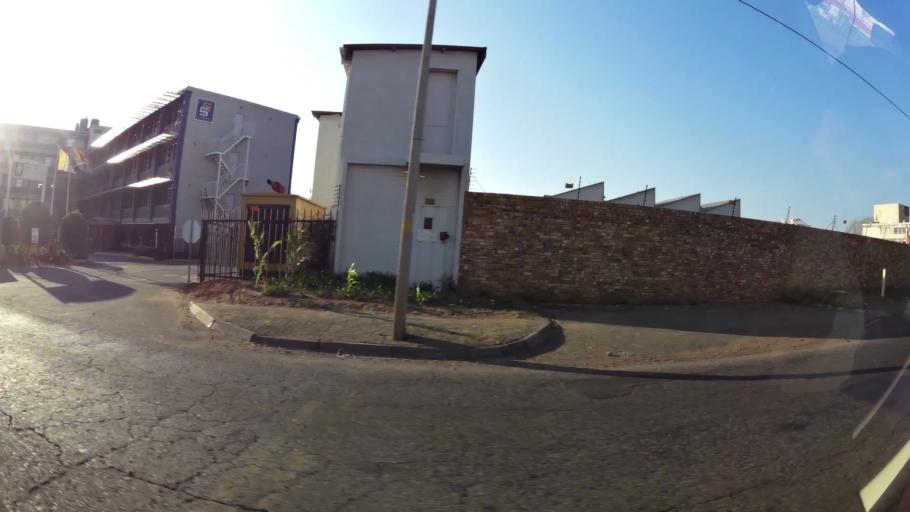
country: ZA
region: Gauteng
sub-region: Ekurhuleni Metropolitan Municipality
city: Germiston
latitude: -26.1662
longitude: 28.1944
